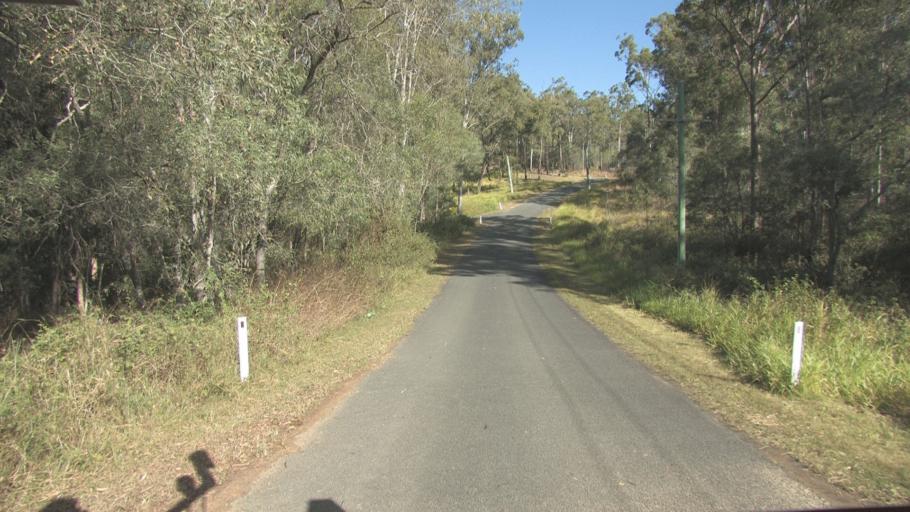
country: AU
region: Queensland
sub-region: Logan
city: Chambers Flat
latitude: -27.8236
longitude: 153.0798
